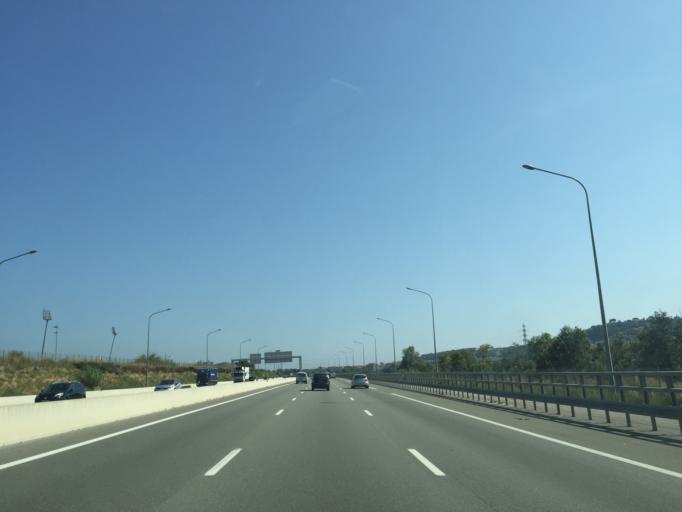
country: FR
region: Provence-Alpes-Cote d'Azur
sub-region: Departement des Alpes-Maritimes
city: Saint-Laurent-du-Var
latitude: 43.6931
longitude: 7.1893
